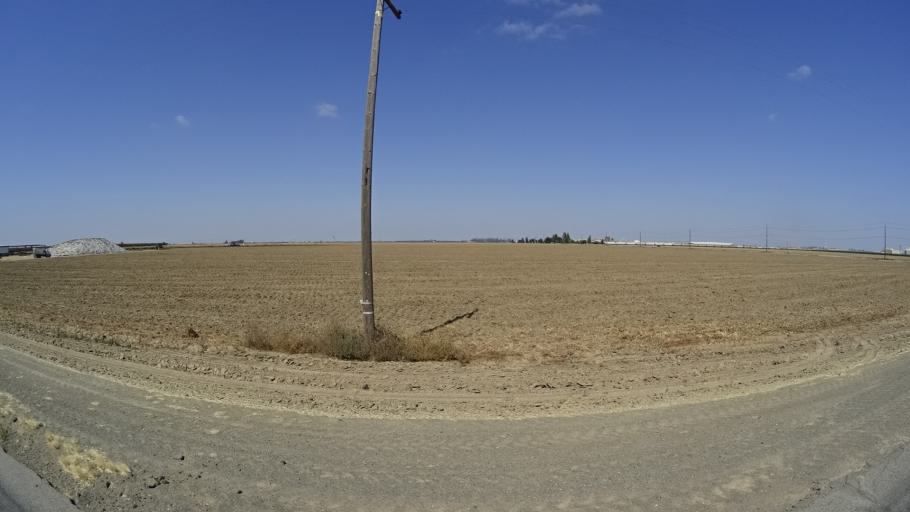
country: US
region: California
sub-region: Kings County
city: Home Garden
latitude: 36.2531
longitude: -119.6369
